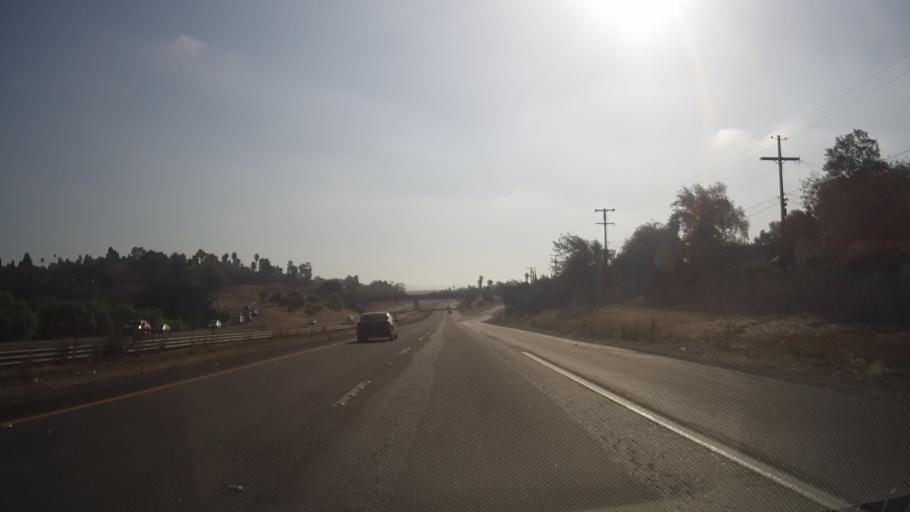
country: US
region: California
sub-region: San Diego County
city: Casa de Oro-Mount Helix
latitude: 32.7462
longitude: -116.9762
